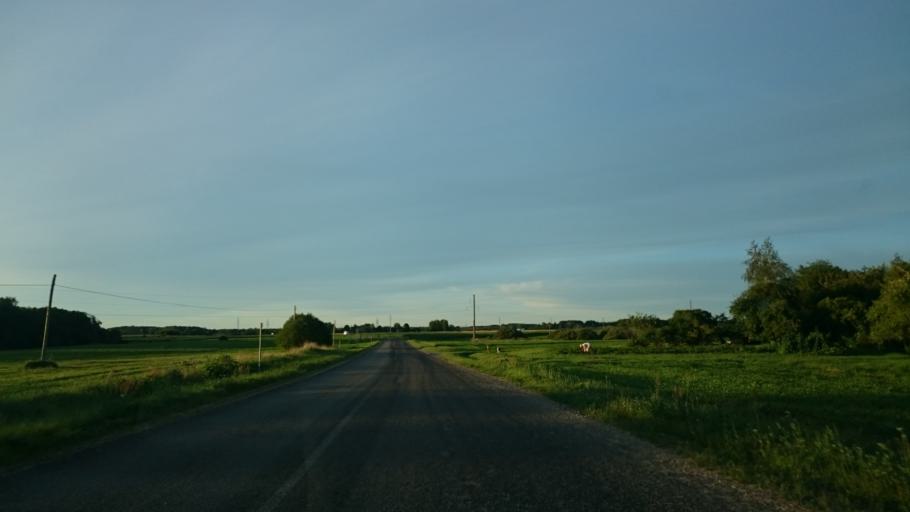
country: LV
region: Saldus Rajons
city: Saldus
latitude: 56.6794
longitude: 22.4983
